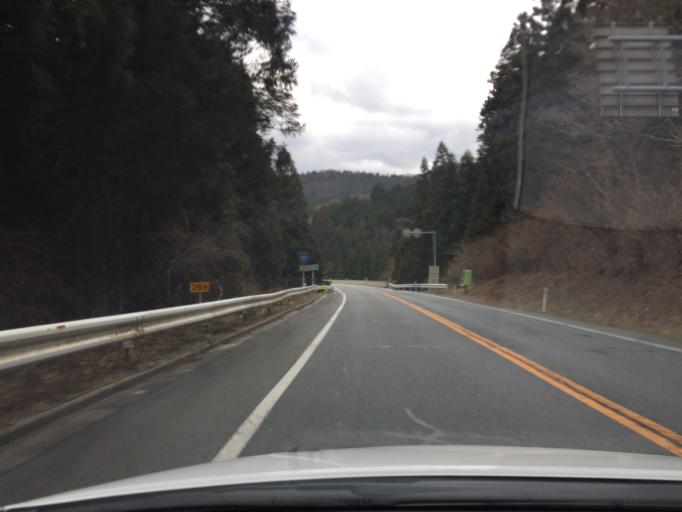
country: JP
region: Fukushima
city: Ishikawa
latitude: 37.1566
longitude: 140.6580
